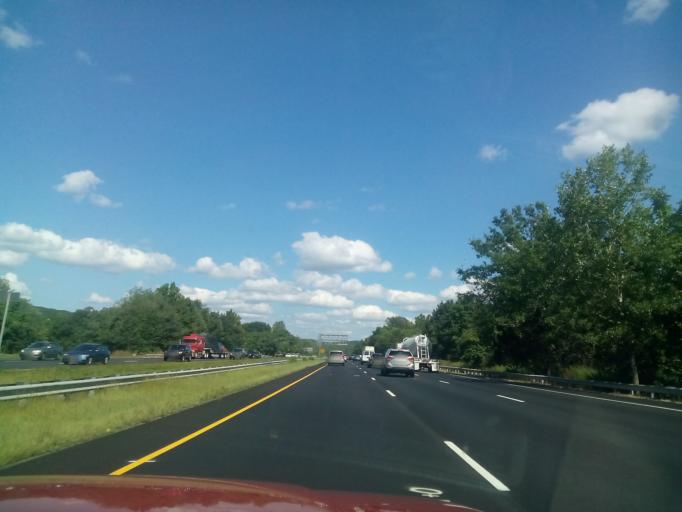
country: US
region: New Jersey
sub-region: Morris County
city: Wharton
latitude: 40.9081
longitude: -74.5776
